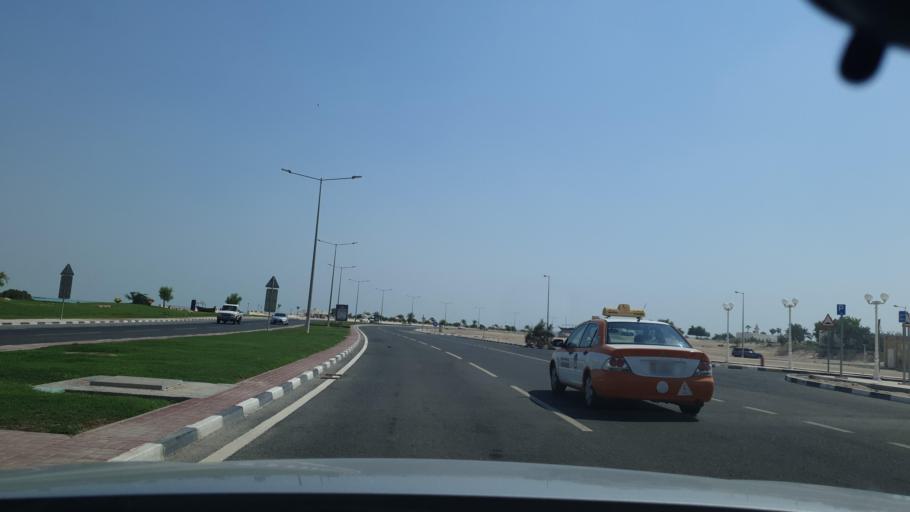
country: QA
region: Al Khawr
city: Al Khawr
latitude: 25.6895
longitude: 51.5028
